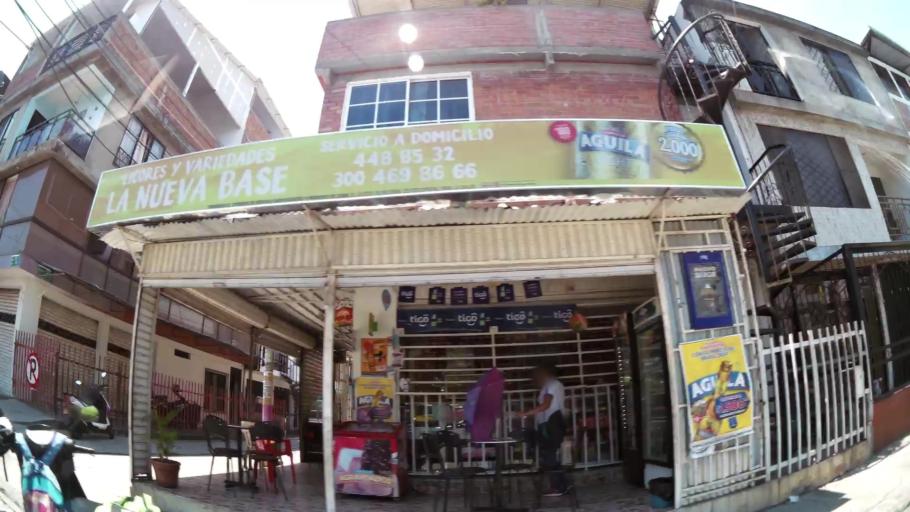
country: CO
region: Valle del Cauca
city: Cali
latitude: 3.4451
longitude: -76.4919
